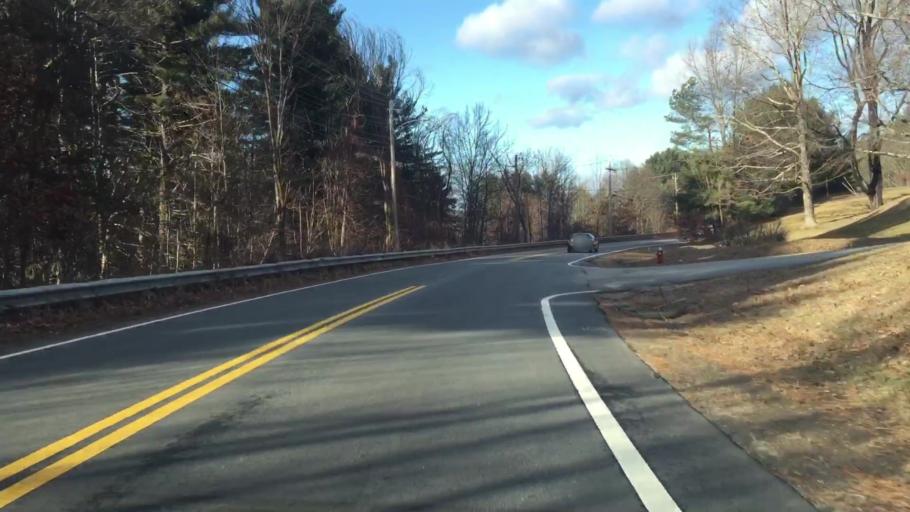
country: US
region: Massachusetts
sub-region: Worcester County
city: West Boylston
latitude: 42.3829
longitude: -71.7889
